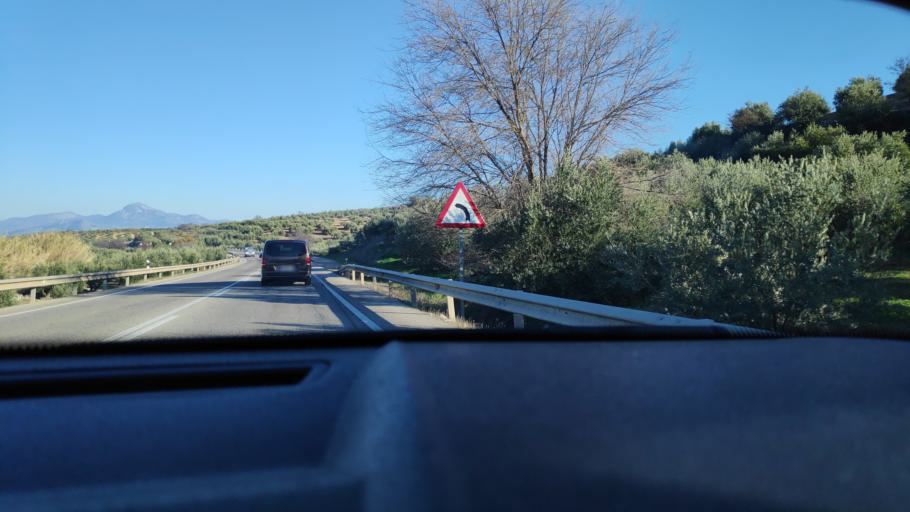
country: ES
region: Andalusia
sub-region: Province of Cordoba
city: Luque
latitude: 37.5673
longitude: -4.2433
